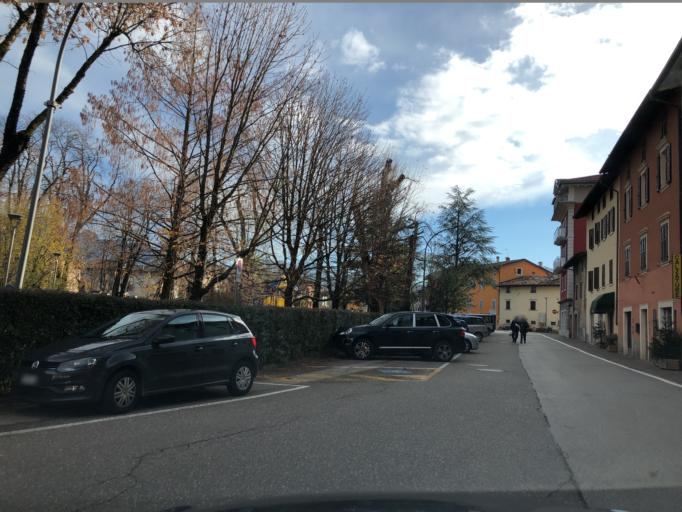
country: IT
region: Trentino-Alto Adige
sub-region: Provincia di Trento
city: Brentonico
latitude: 45.8182
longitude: 10.9548
